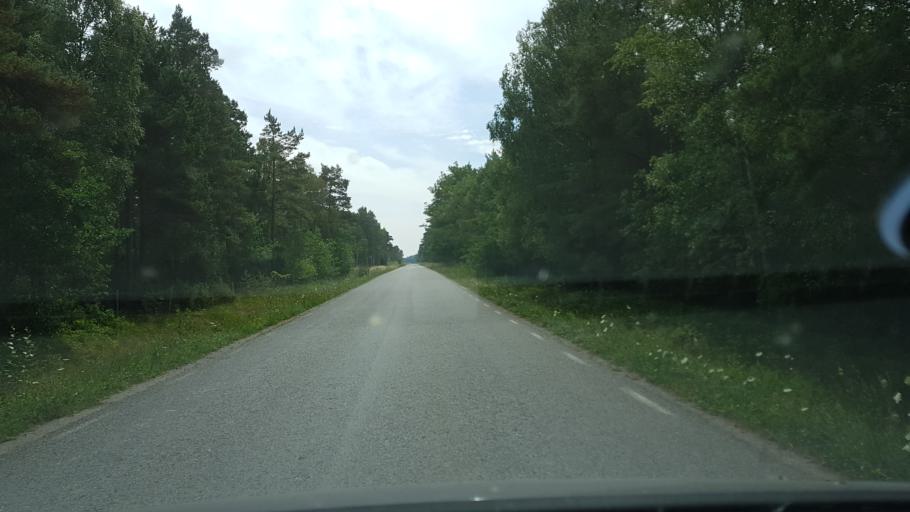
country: SE
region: Gotland
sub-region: Gotland
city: Visby
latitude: 57.7157
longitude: 18.5091
